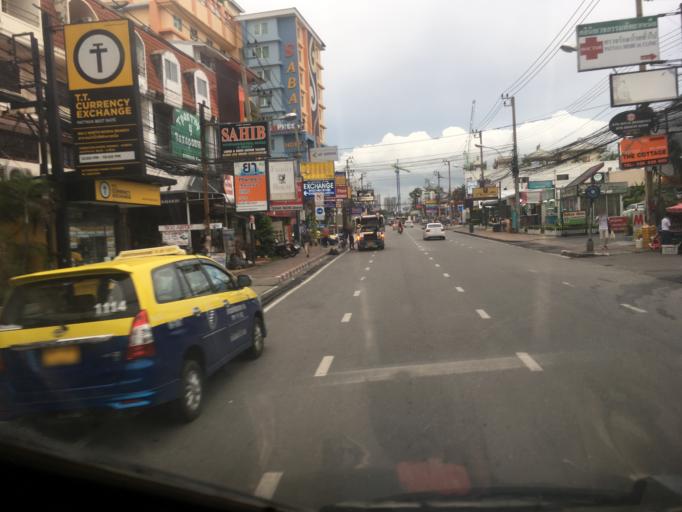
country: TH
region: Chon Buri
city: Phatthaya
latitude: 12.9464
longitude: 100.8889
